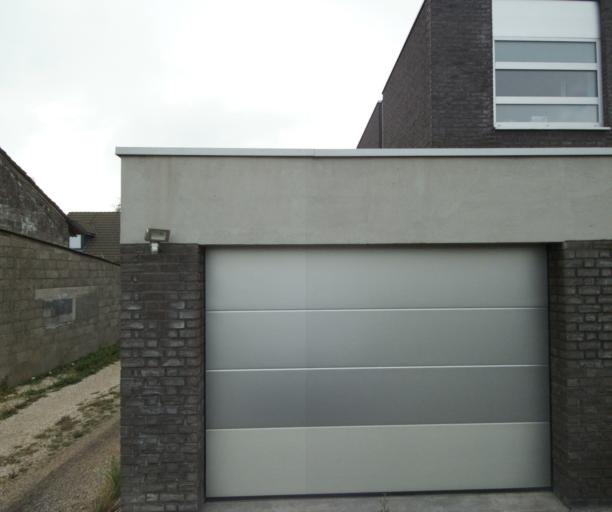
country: FR
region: Nord-Pas-de-Calais
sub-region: Departement du Nord
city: Wasquehal
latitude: 50.6678
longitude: 3.1199
